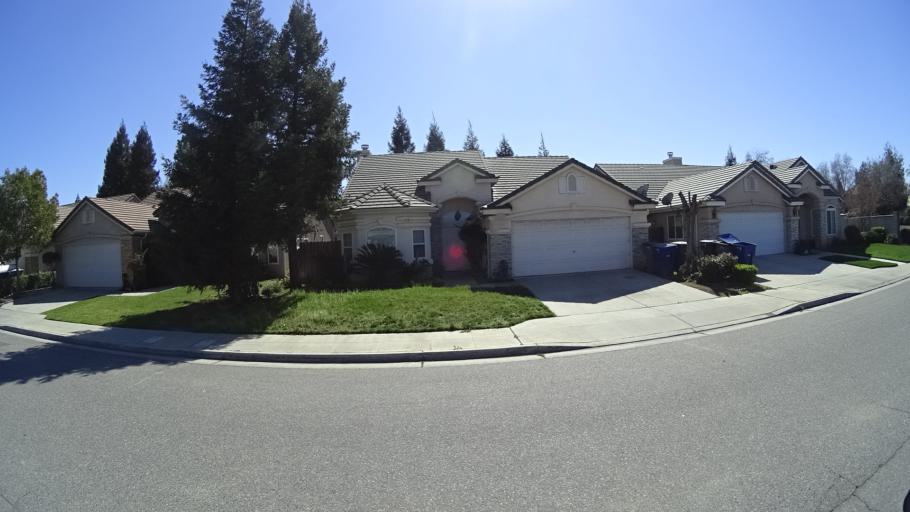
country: US
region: California
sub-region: Fresno County
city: Clovis
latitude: 36.8780
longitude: -119.7383
